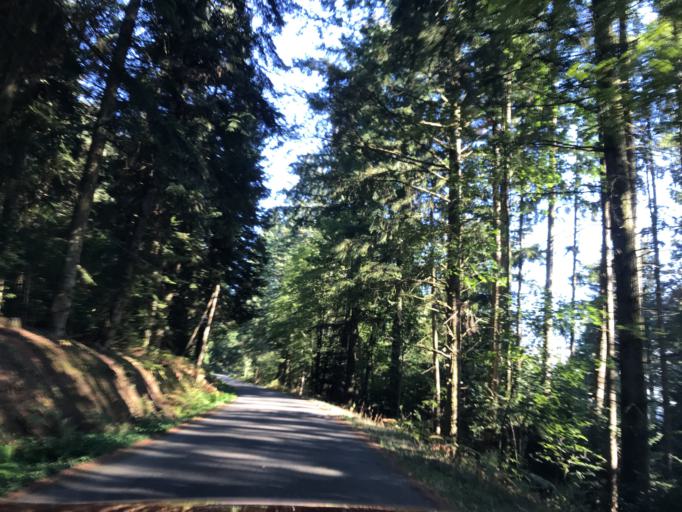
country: FR
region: Auvergne
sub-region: Departement du Puy-de-Dome
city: Escoutoux
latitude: 45.7723
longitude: 3.6147
